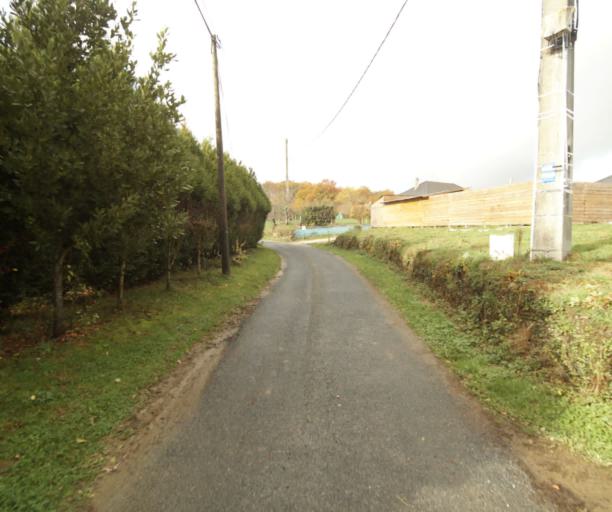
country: FR
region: Limousin
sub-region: Departement de la Correze
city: Sainte-Fereole
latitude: 45.2106
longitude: 1.6267
